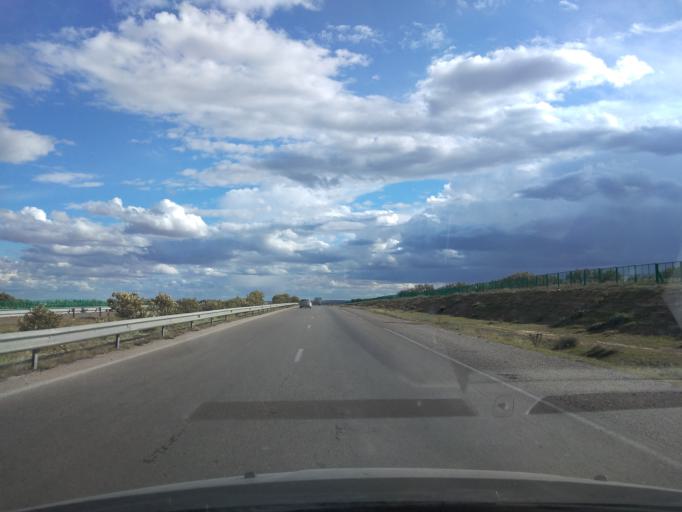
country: TN
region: Al Munastir
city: Manzil Kamil
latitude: 35.5474
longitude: 10.6205
